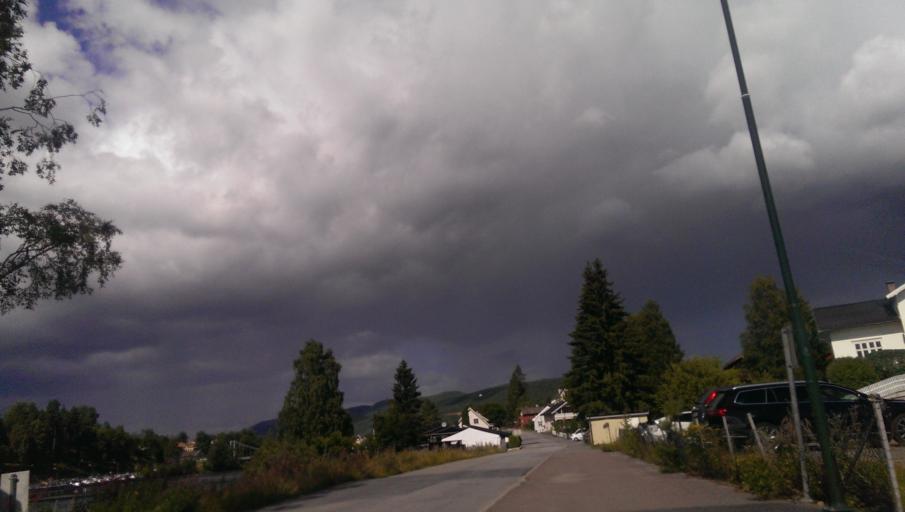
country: NO
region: Buskerud
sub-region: Kongsberg
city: Kongsberg
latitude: 59.6581
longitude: 9.6533
